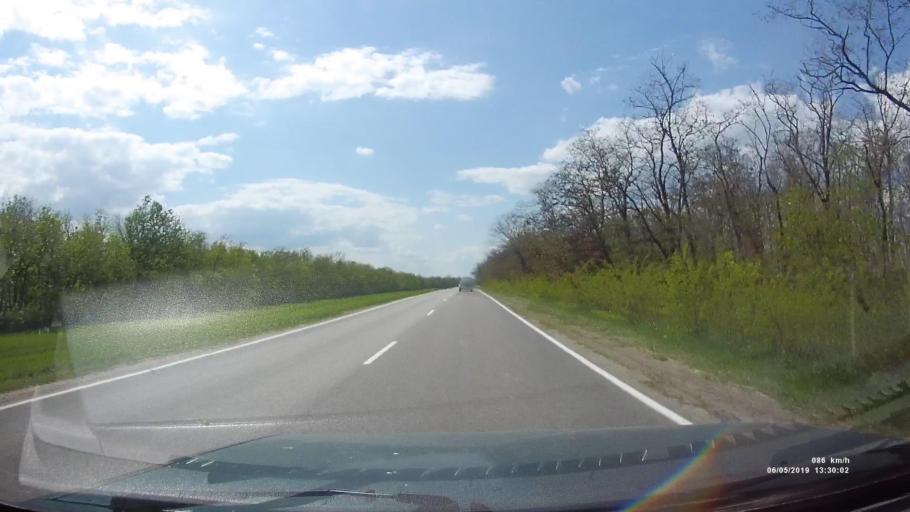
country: RU
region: Rostov
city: Ust'-Donetskiy
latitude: 47.6712
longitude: 40.8335
